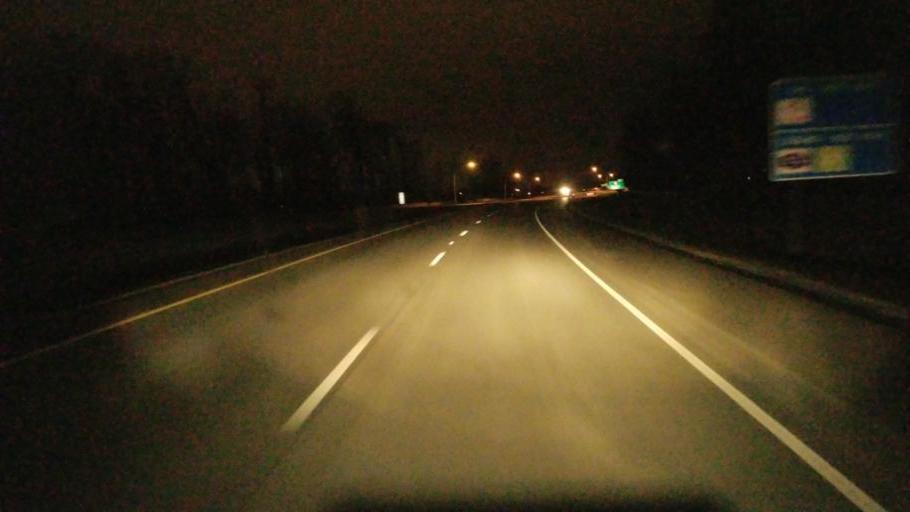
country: US
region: Ohio
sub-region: Franklin County
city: New Albany
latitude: 40.0824
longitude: -82.7917
